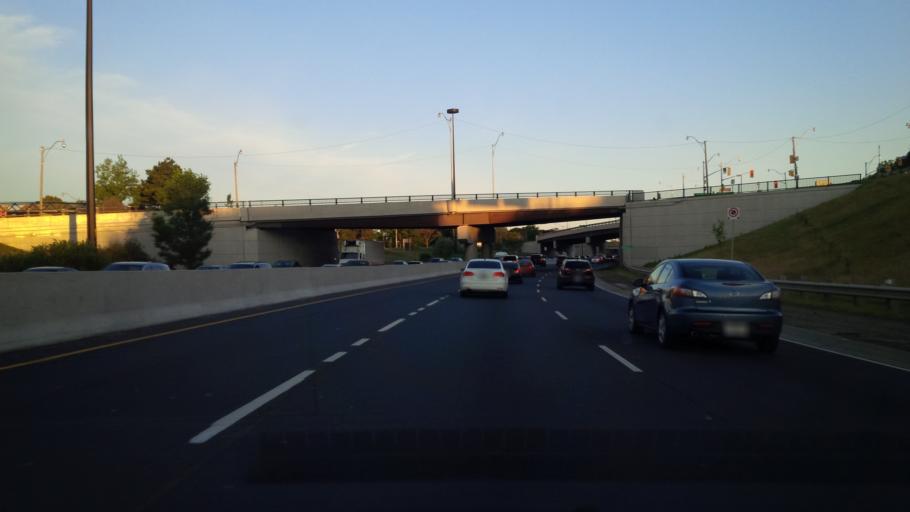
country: CA
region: Ontario
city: Toronto
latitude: 43.6327
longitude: -79.4334
